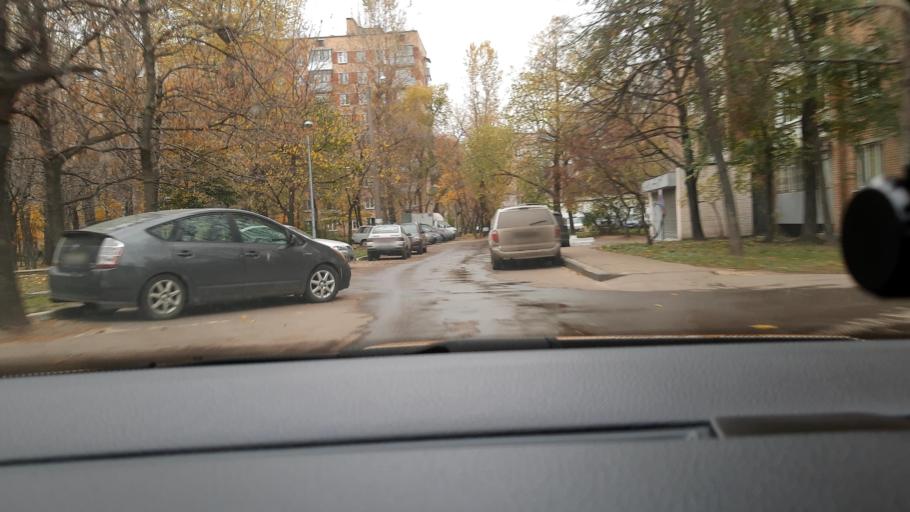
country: RU
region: Moscow
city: Kolomenskoye
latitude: 55.6845
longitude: 37.6804
